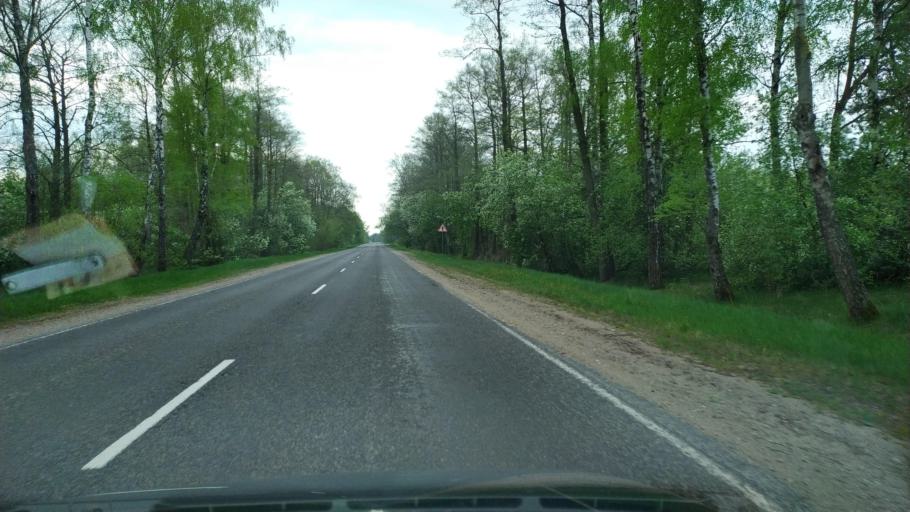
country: BY
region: Brest
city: Zhabinka
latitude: 52.2452
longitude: 23.9738
